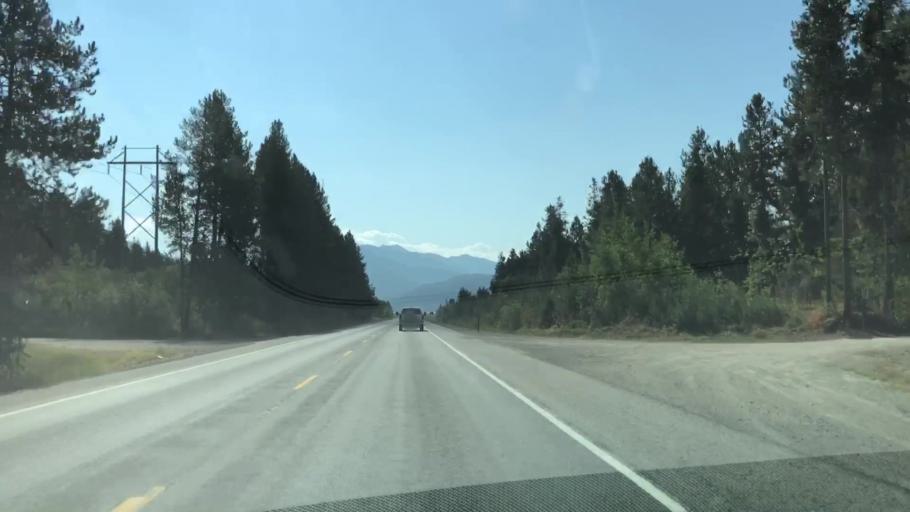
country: US
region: Wyoming
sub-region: Teton County
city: Hoback
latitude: 43.1974
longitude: -111.0411
